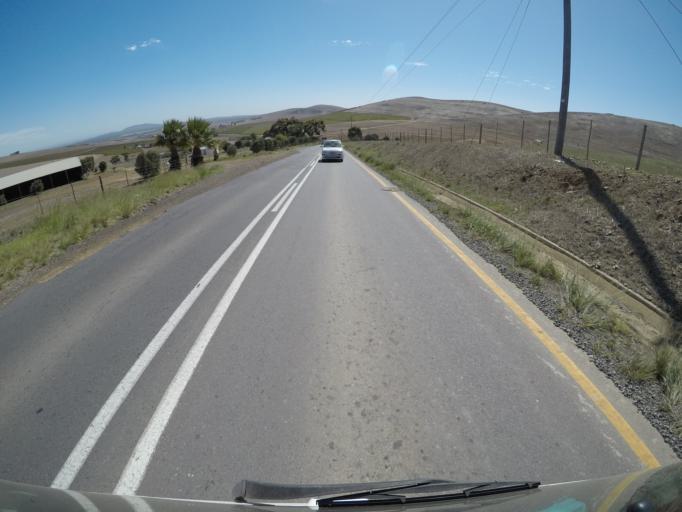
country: ZA
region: Western Cape
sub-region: City of Cape Town
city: Kraaifontein
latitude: -33.7950
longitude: 18.6058
